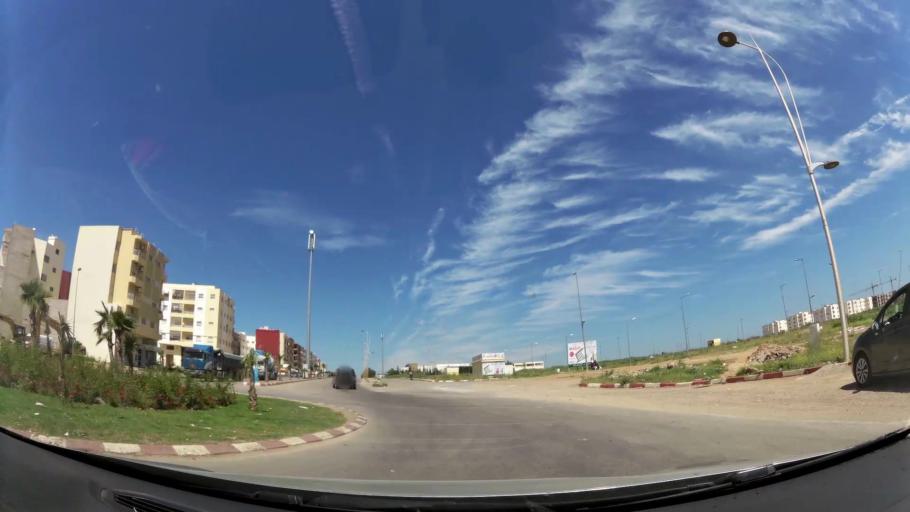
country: MA
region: Fes-Boulemane
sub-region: Fes
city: Fes
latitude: 33.9997
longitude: -4.9793
